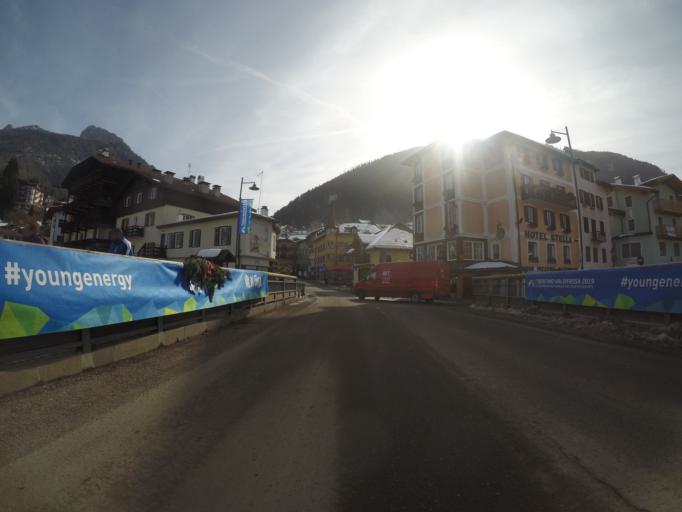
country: IT
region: Trentino-Alto Adige
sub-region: Provincia di Trento
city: Moena
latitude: 46.3766
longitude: 11.6604
